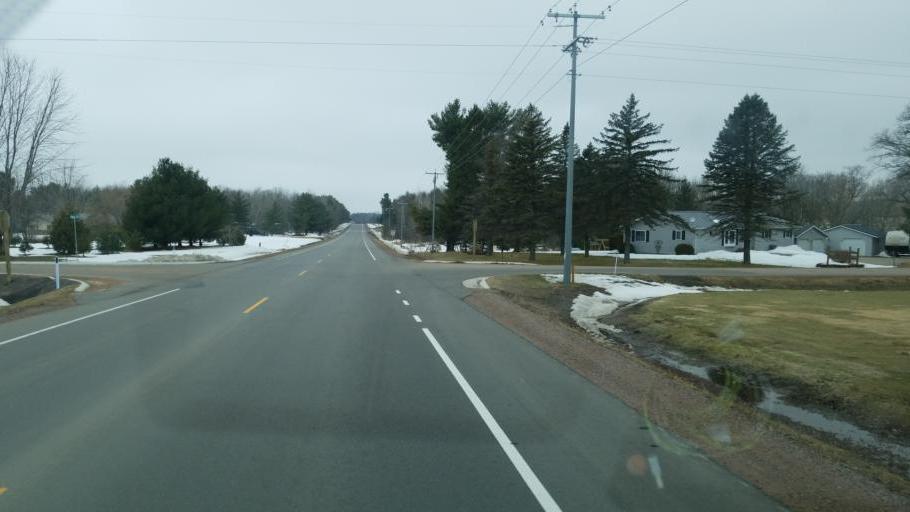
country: US
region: Wisconsin
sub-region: Wood County
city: Marshfield
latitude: 44.6561
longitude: -90.2382
